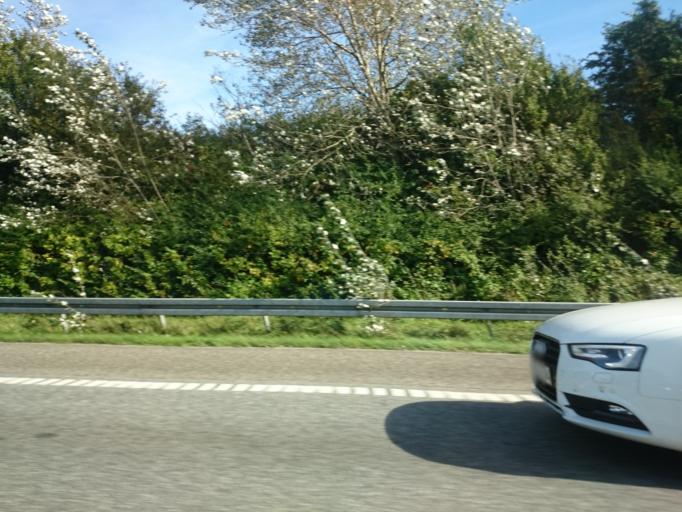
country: DK
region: Central Jutland
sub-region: Skanderborg Kommune
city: Skanderborg
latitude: 56.0279
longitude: 9.8817
